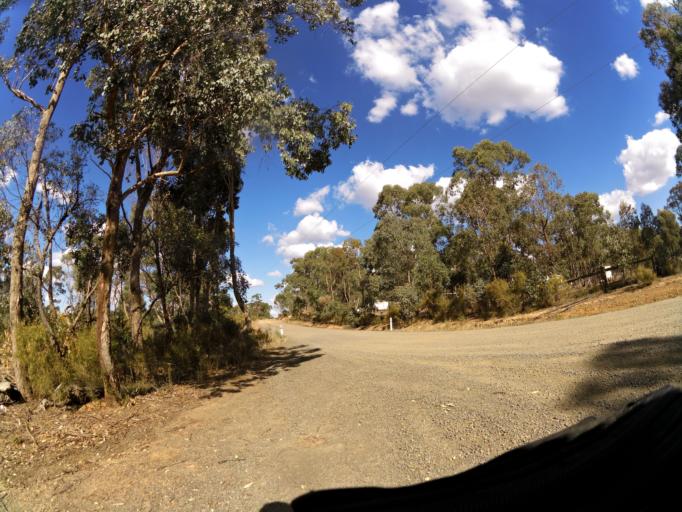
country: AU
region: Victoria
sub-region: Greater Bendigo
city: Kennington
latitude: -36.9525
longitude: 144.7757
